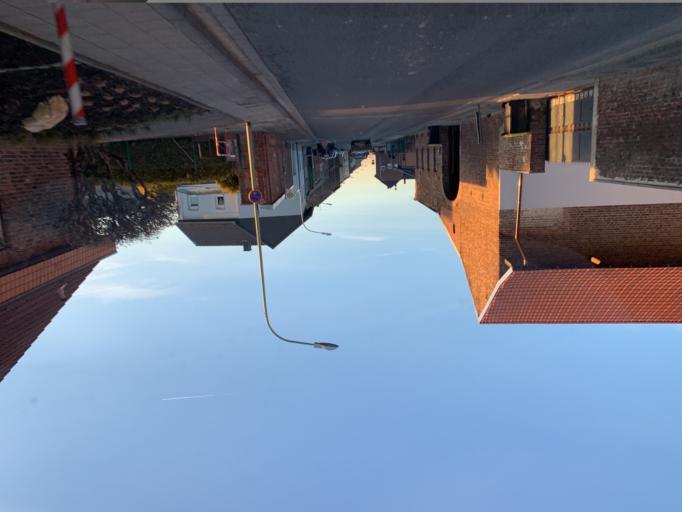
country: DE
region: North Rhine-Westphalia
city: Julich
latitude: 50.9612
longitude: 6.3794
